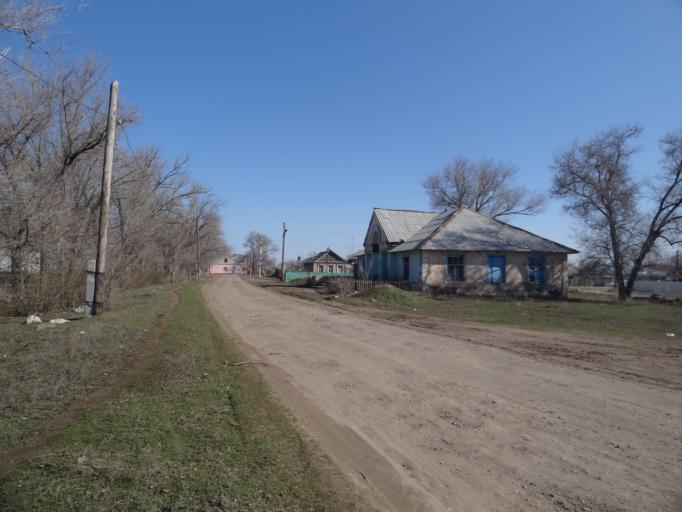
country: RU
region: Saratov
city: Shumeyka
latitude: 51.3892
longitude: 46.2989
